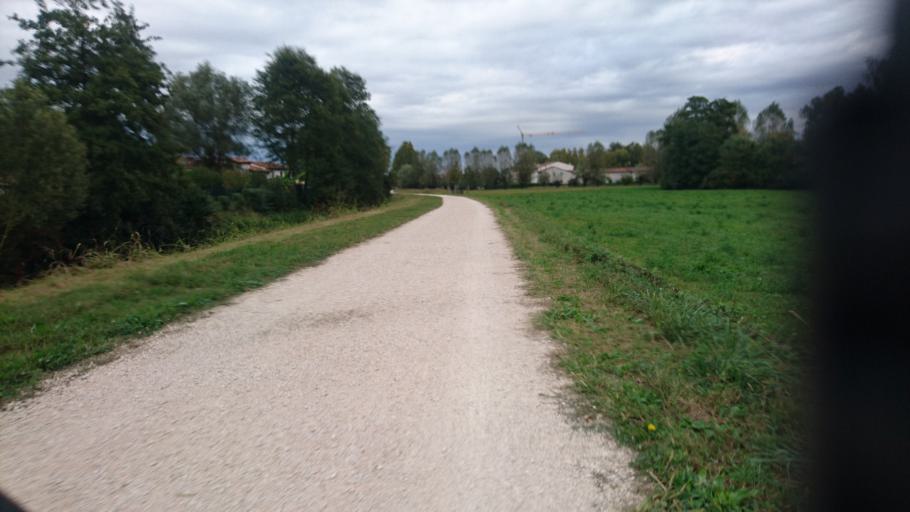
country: IT
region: Veneto
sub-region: Provincia di Vicenza
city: Creazzo
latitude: 45.5302
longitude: 11.4646
